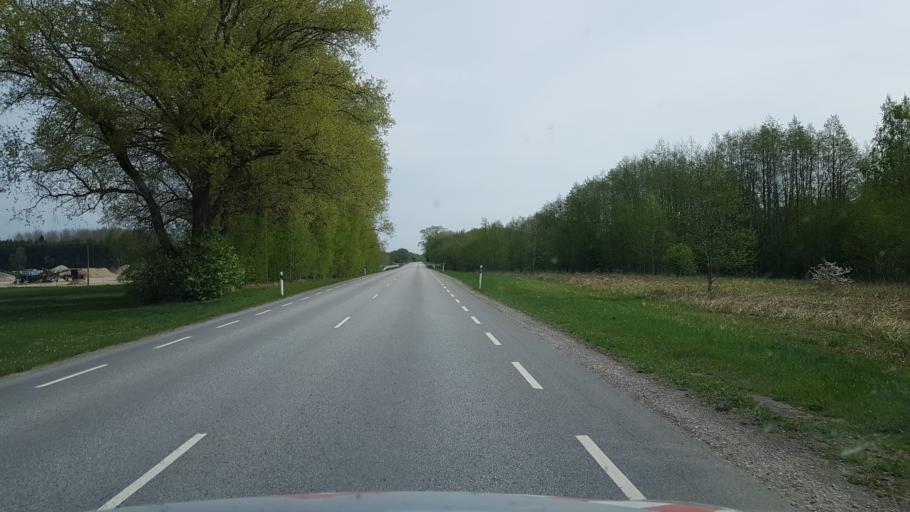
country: EE
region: Paernumaa
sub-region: Sauga vald
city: Sauga
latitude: 58.4352
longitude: 24.4516
